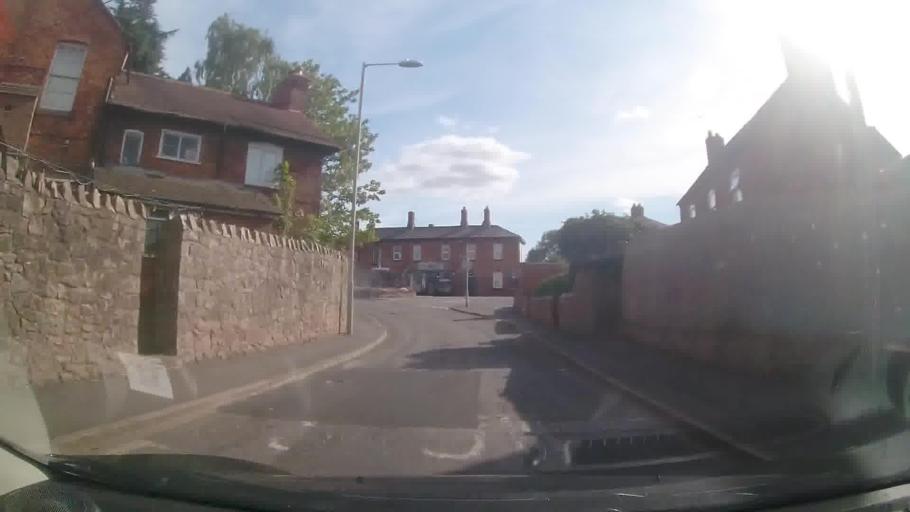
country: GB
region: England
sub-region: Shropshire
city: Pontesbury
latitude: 52.6495
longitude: -2.8866
